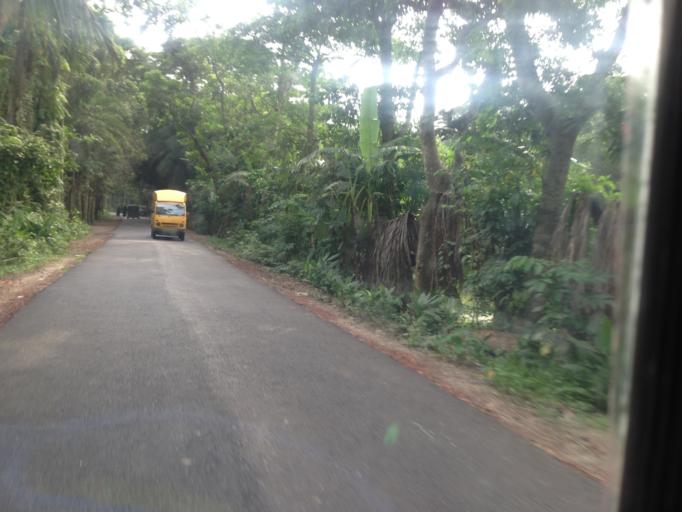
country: BD
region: Chittagong
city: Raipur
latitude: 23.0372
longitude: 90.7257
